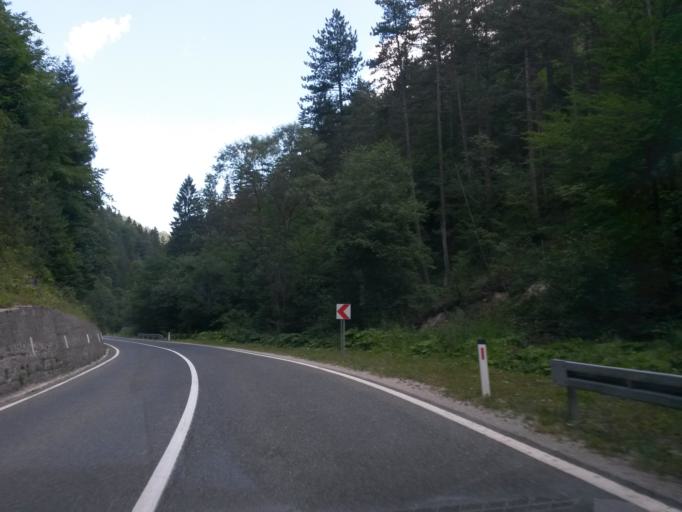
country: BA
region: Federation of Bosnia and Herzegovina
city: Bugojno
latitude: 44.0300
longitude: 17.3699
